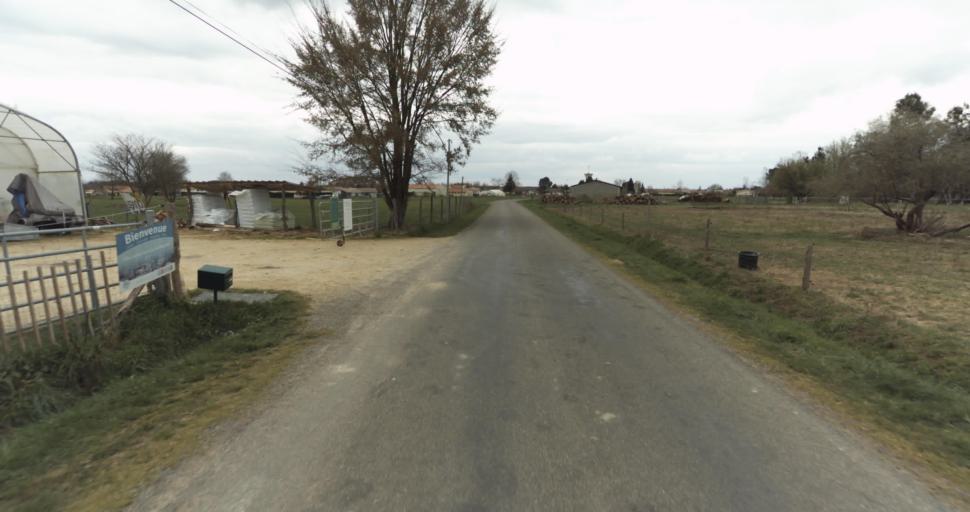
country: FR
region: Aquitaine
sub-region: Departement des Landes
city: Roquefort
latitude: 44.0216
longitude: -0.3311
